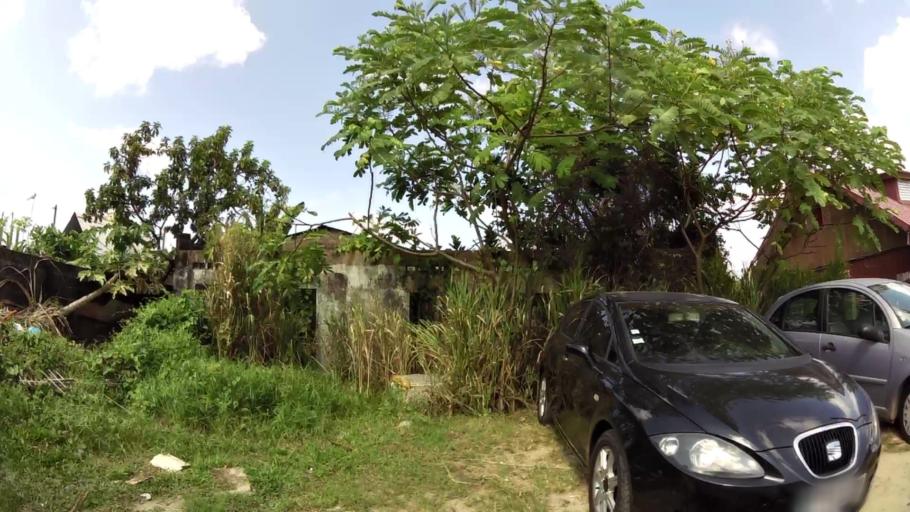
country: GF
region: Guyane
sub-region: Guyane
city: Cayenne
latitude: 4.9262
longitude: -52.3163
